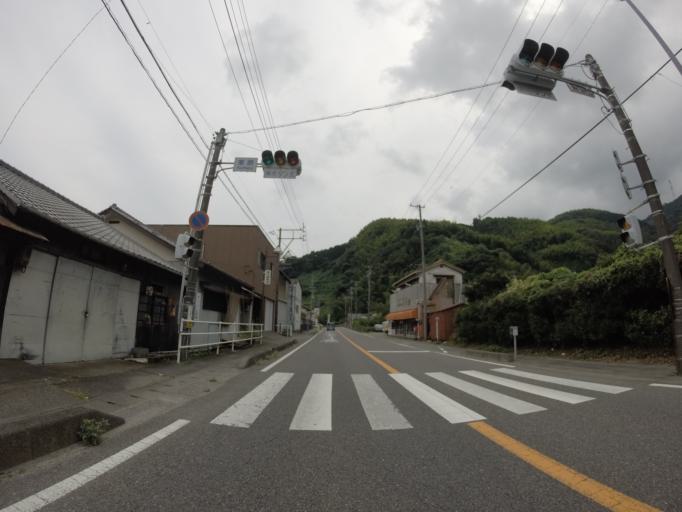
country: JP
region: Shizuoka
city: Shizuoka-shi
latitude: 35.0821
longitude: 138.5147
